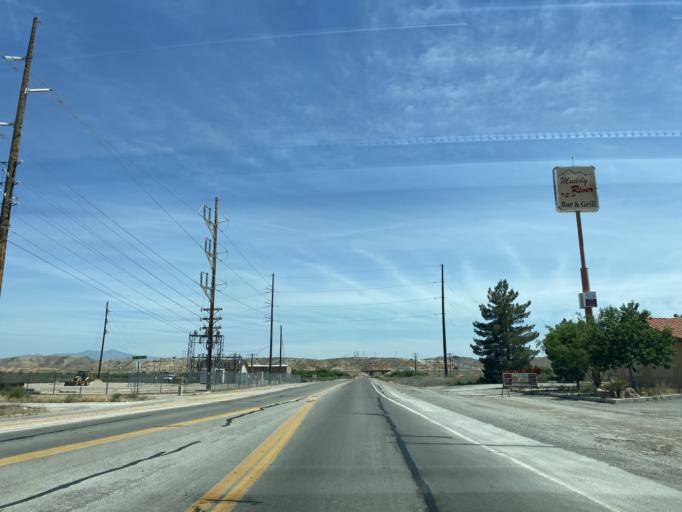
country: US
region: Nevada
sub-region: Clark County
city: Moapa Town
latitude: 36.6643
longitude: -114.5803
